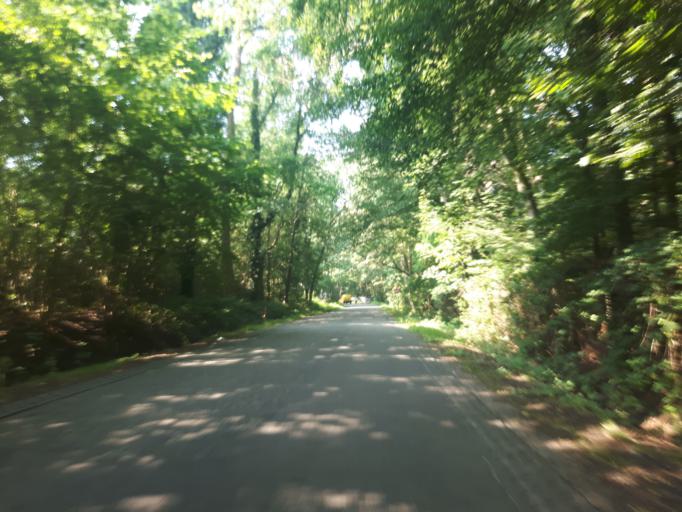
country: NL
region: Overijssel
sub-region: Gemeente Haaksbergen
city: Haaksbergen
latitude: 52.1927
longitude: 6.7837
